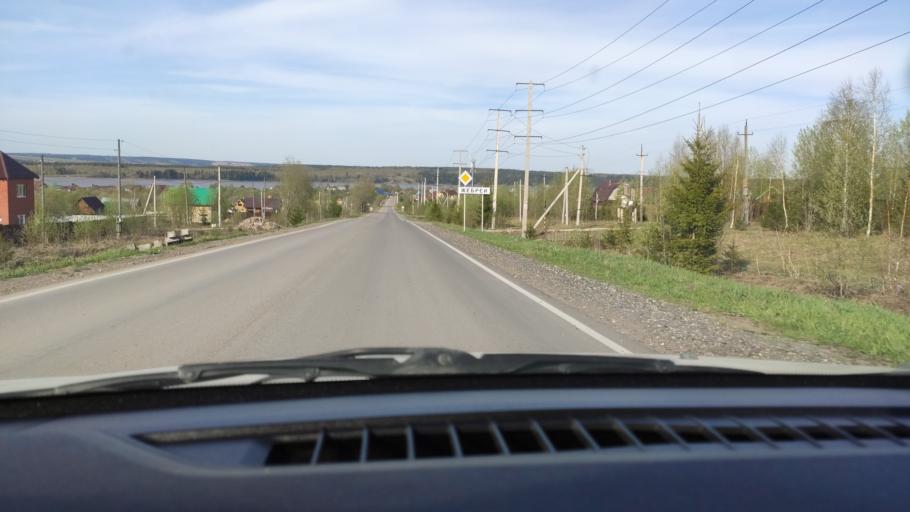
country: RU
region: Perm
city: Sylva
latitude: 57.9261
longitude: 56.6836
